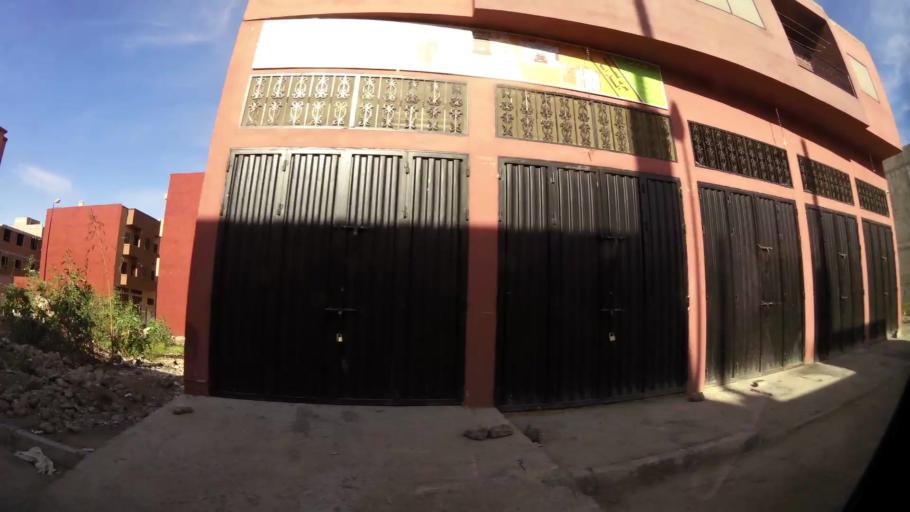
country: MA
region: Marrakech-Tensift-Al Haouz
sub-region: Marrakech
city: Marrakesh
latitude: 31.6800
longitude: -8.0451
